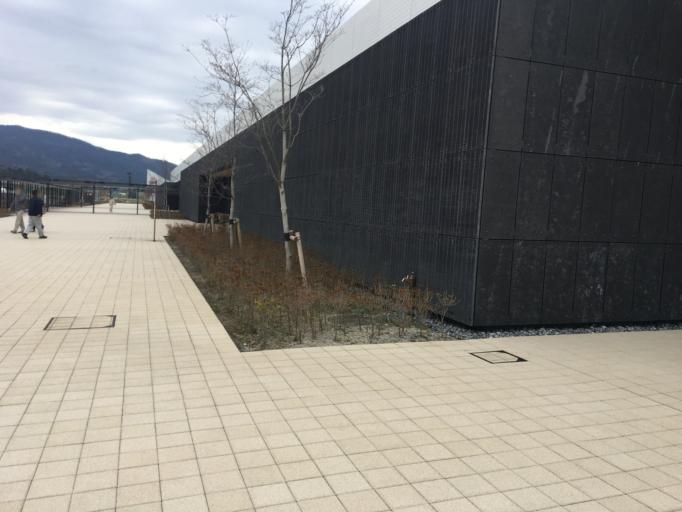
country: JP
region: Iwate
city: Ofunato
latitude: 39.0070
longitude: 141.6261
